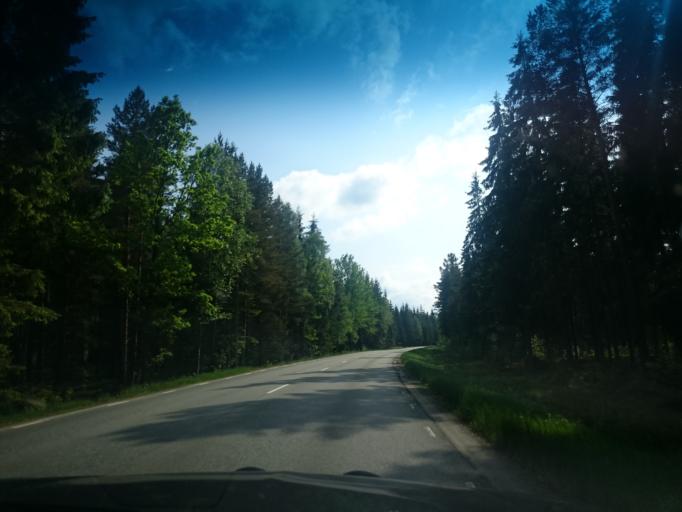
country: SE
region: Joenkoeping
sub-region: Vetlanda Kommun
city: Vetlanda
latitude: 57.4077
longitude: 15.0016
